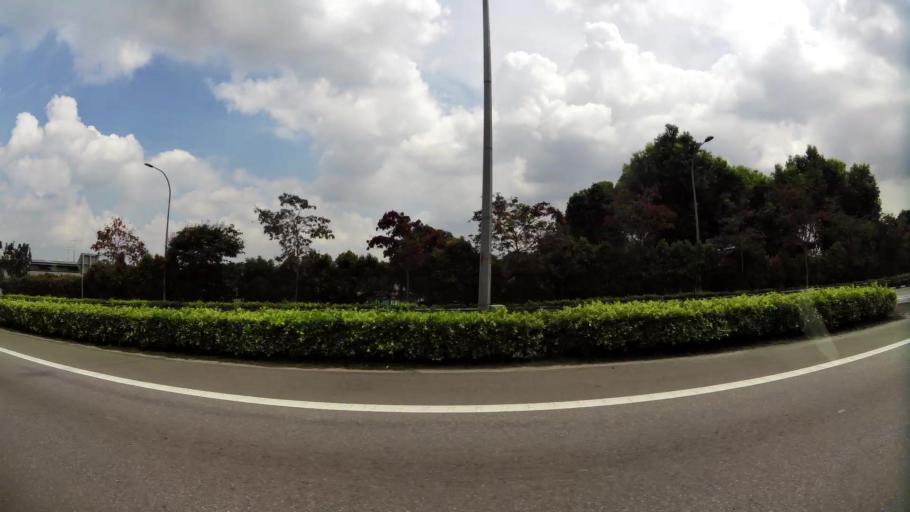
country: SG
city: Singapore
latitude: 1.3731
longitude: 103.8598
